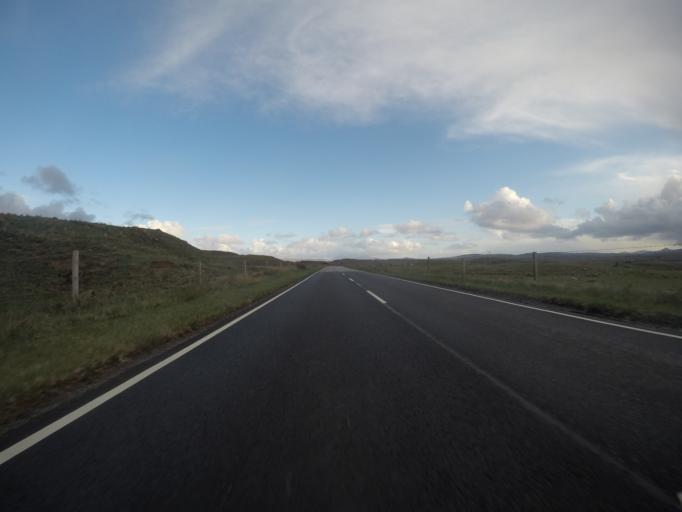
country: GB
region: Scotland
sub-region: Highland
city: Portree
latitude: 57.5402
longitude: -6.3635
